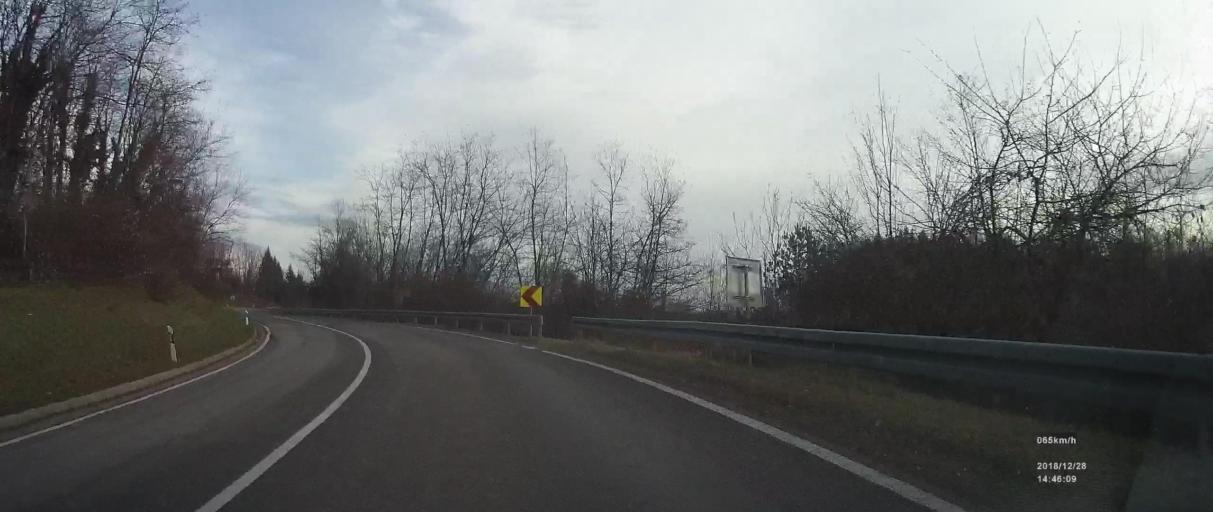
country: SI
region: Crnomelj
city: Crnomelj
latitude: 45.4488
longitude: 15.3125
